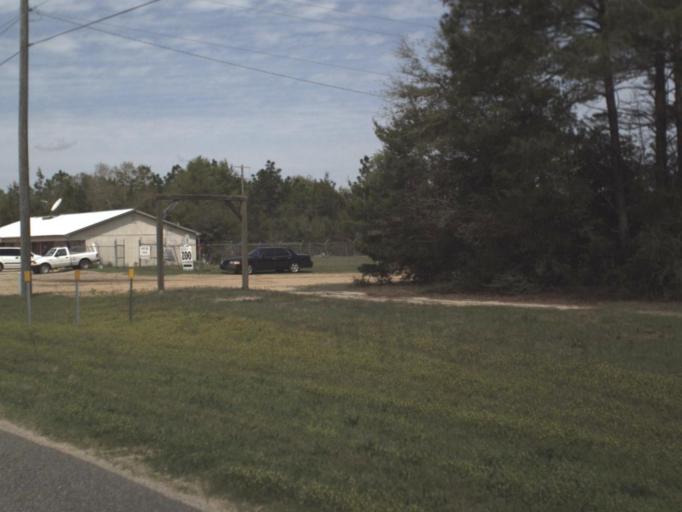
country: US
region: Florida
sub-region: Okaloosa County
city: Crestview
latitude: 30.7514
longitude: -86.4436
